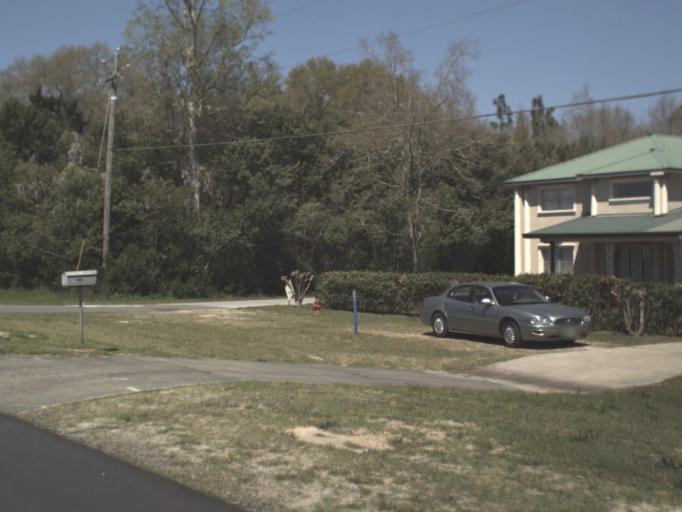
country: US
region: Florida
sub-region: Walton County
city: DeFuniak Springs
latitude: 30.7354
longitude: -86.1560
